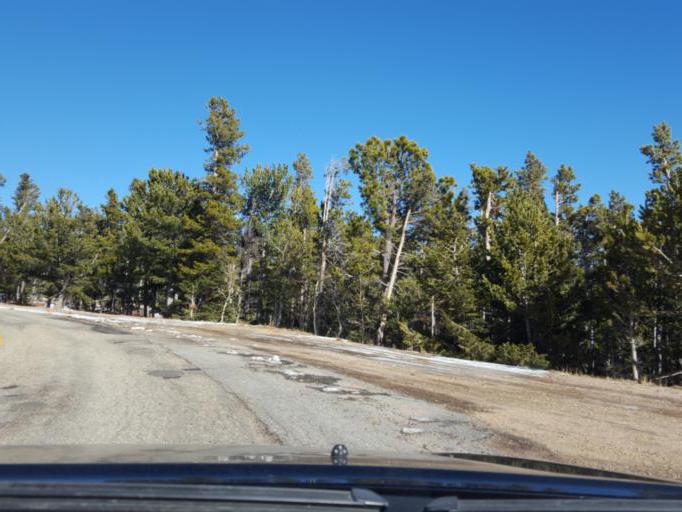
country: US
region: Colorado
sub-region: Boulder County
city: Nederland
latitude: 40.0765
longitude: -105.5054
